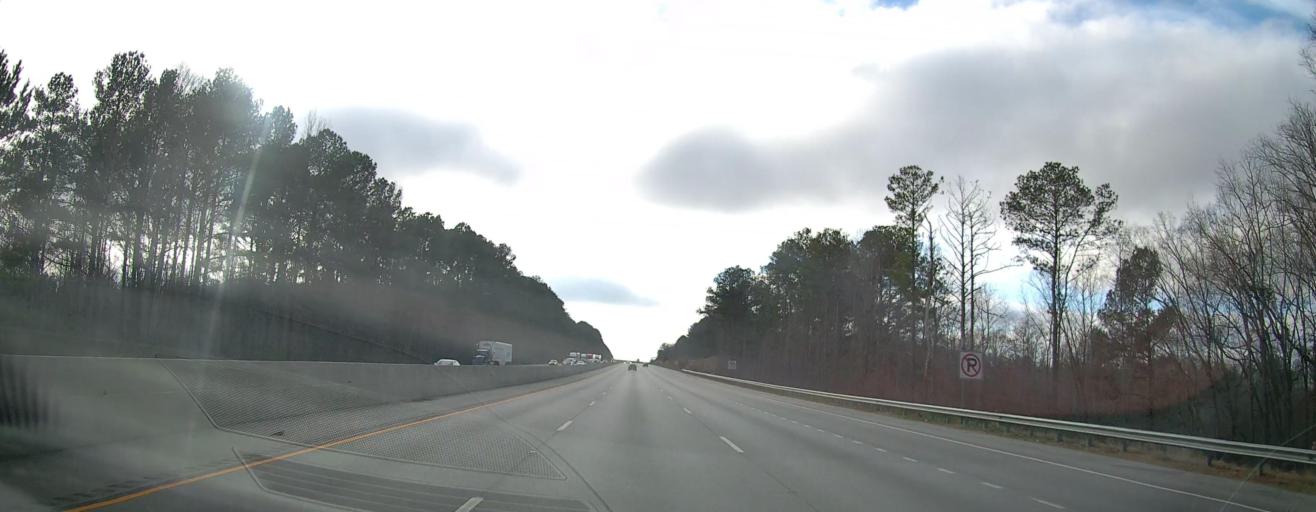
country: US
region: Georgia
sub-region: Haralson County
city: Tallapoosa
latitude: 33.6664
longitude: -85.3741
